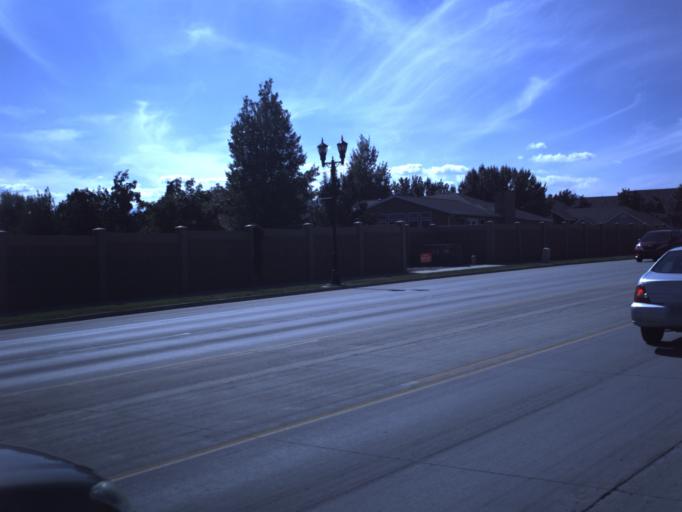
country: US
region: Utah
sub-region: Salt Lake County
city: South Jordan Heights
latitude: 40.5624
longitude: -111.9544
